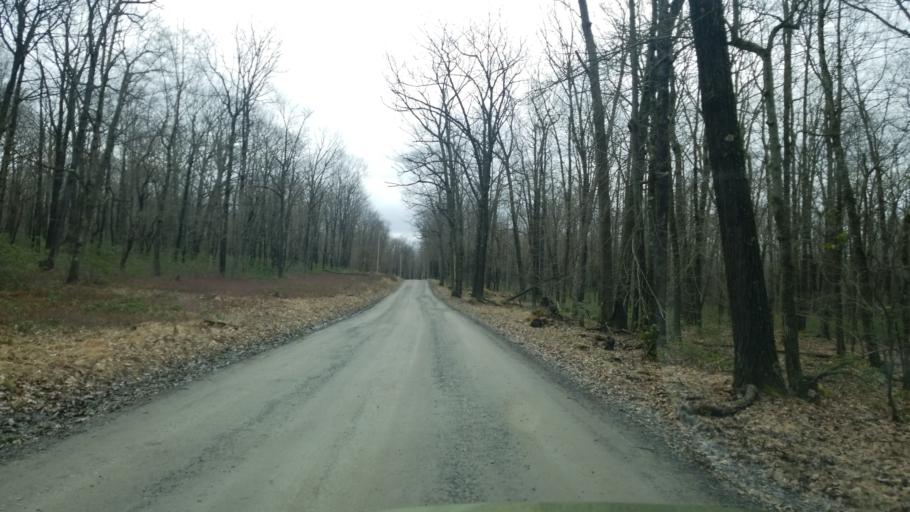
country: US
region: Pennsylvania
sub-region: Clearfield County
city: Shiloh
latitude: 41.1758
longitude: -78.3133
